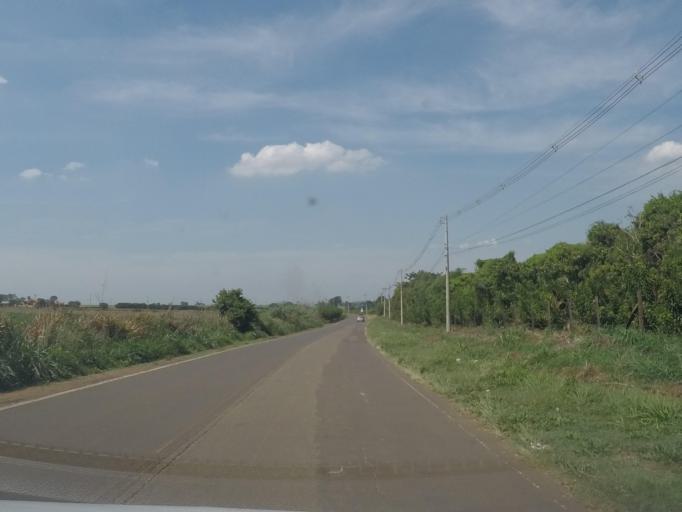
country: BR
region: Sao Paulo
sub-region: Monte Mor
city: Monte Mor
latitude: -22.8801
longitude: -47.3023
